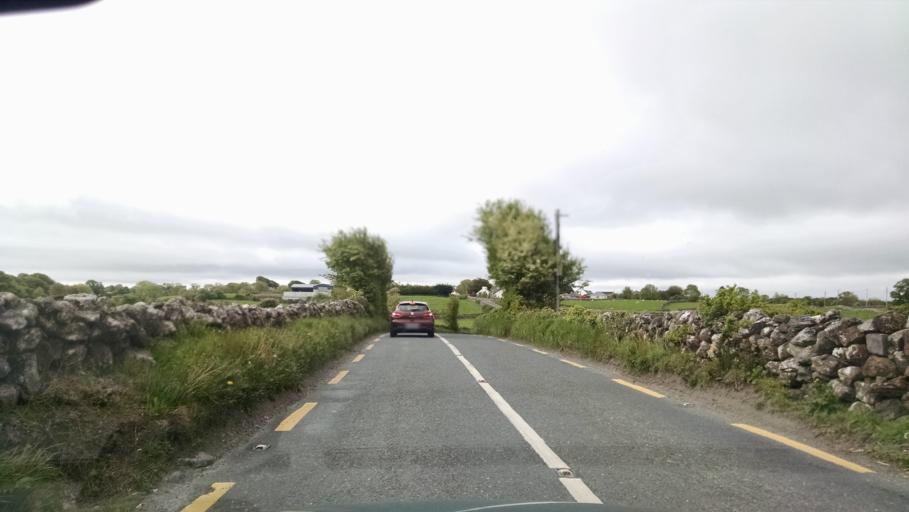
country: IE
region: Connaught
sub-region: County Galway
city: Moycullen
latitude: 53.4852
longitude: -9.0873
